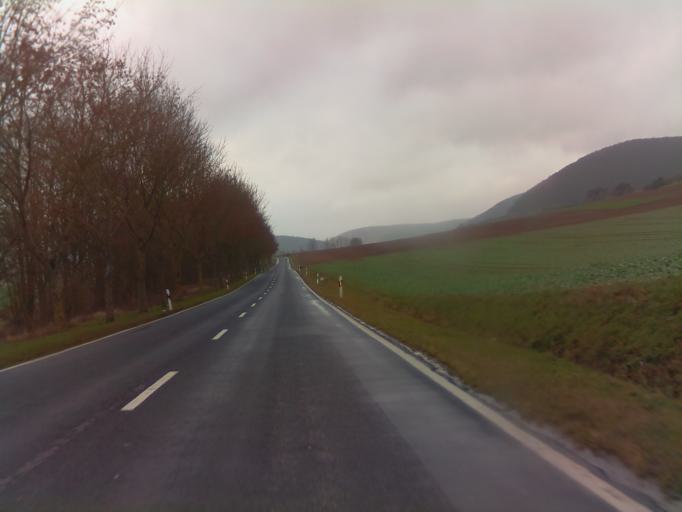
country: DE
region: Thuringia
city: Juchsen
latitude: 50.4686
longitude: 10.5311
